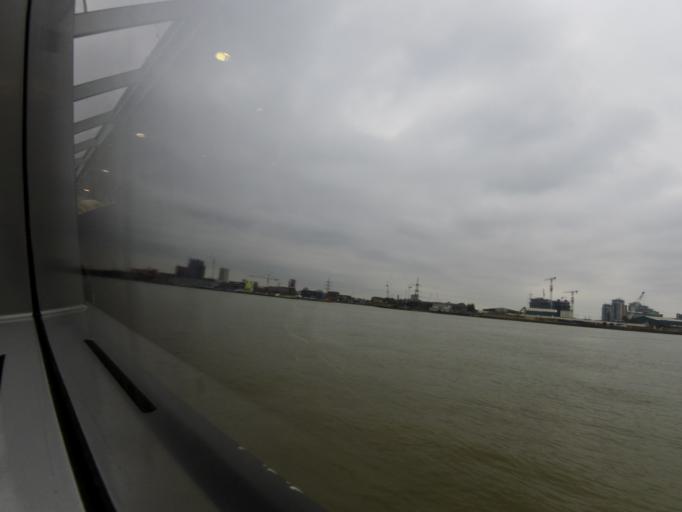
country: GB
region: England
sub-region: Greater London
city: Poplar
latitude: 51.5039
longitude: 0.0077
